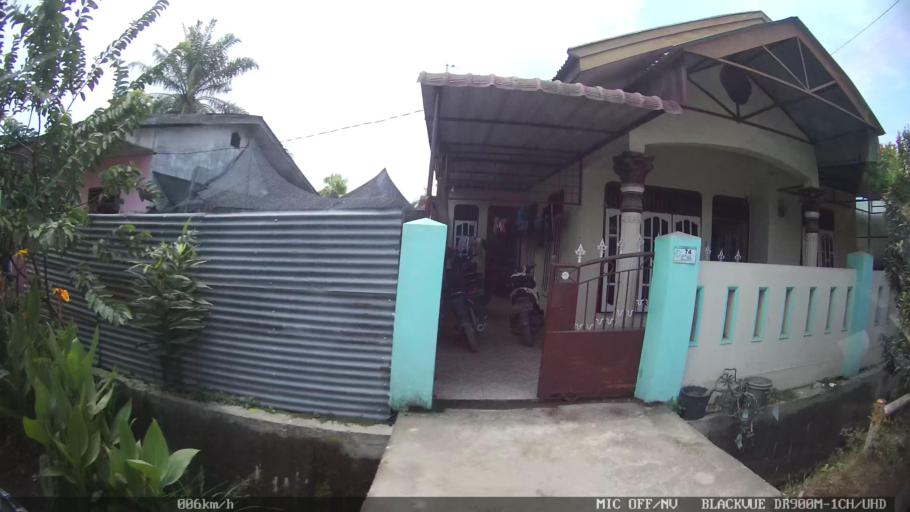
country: ID
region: North Sumatra
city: Perbaungan
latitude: 3.5411
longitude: 98.8813
